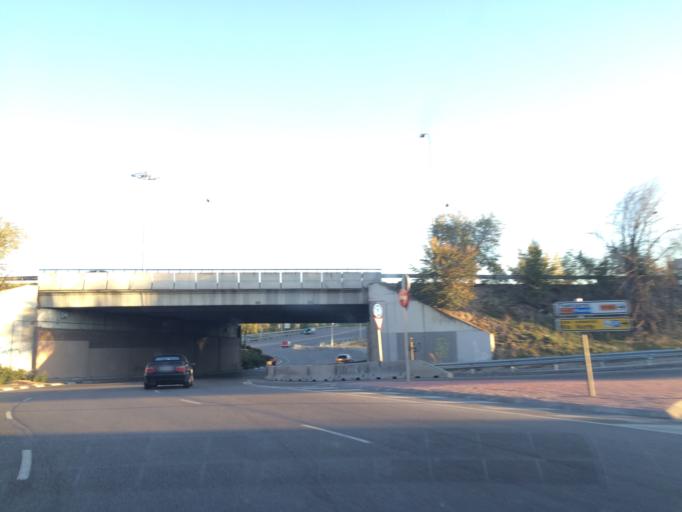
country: ES
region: Madrid
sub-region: Provincia de Madrid
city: Alcobendas
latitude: 40.5351
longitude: -3.6416
